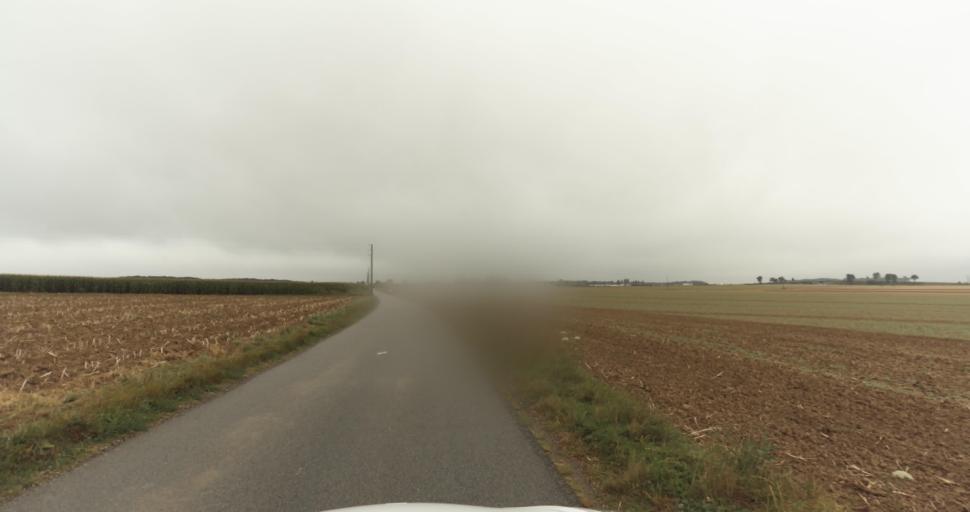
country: FR
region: Haute-Normandie
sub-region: Departement de l'Eure
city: Normanville
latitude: 49.0807
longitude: 1.1967
